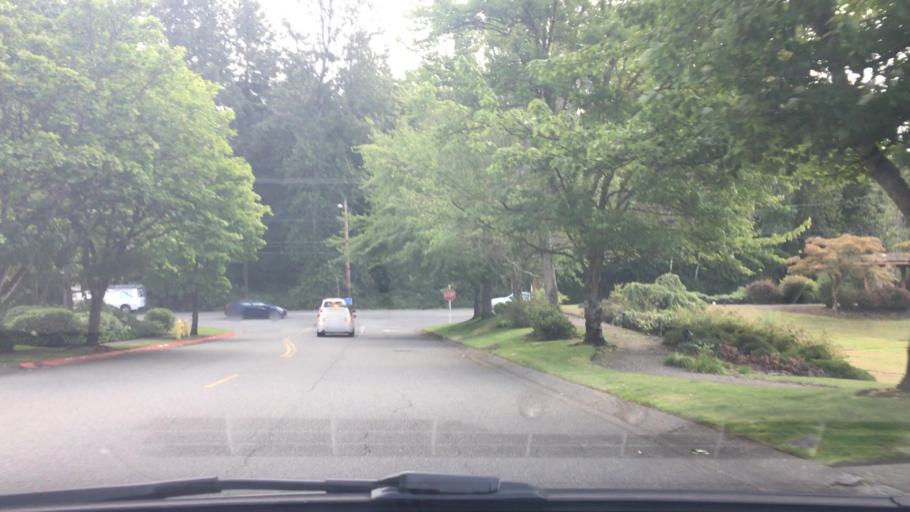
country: US
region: Washington
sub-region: King County
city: City of Sammamish
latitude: 47.5749
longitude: -122.0367
